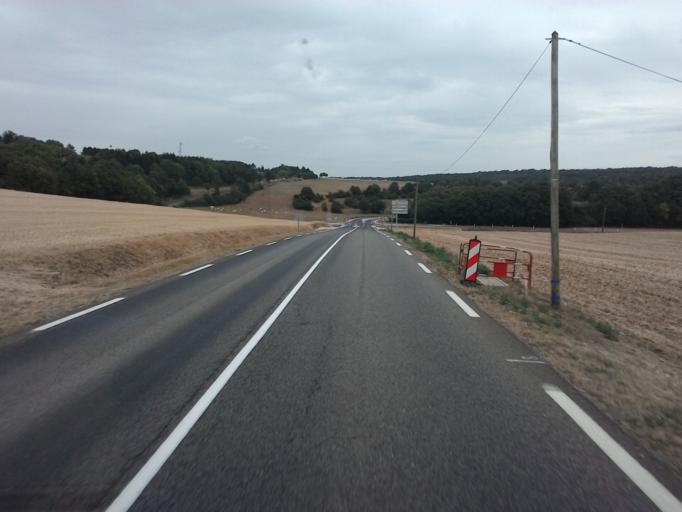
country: FR
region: Lorraine
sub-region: Departement de Meurthe-et-Moselle
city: Colombey-les-Belles
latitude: 48.5702
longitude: 5.9575
